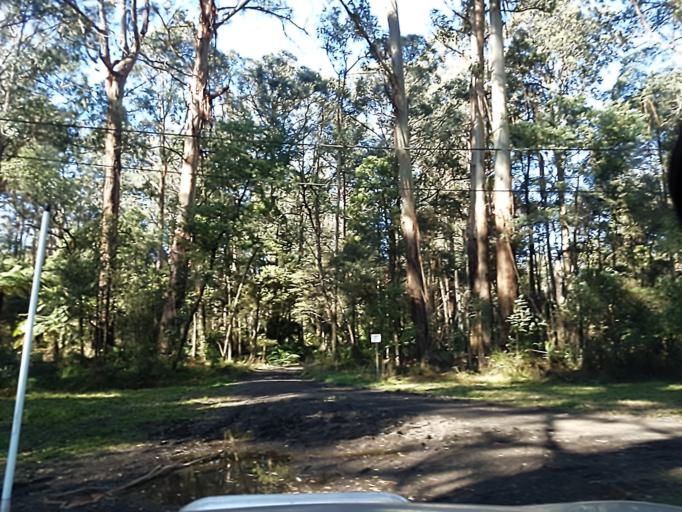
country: AU
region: Victoria
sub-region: Yarra Ranges
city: Healesville
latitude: -37.5346
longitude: 145.4729
